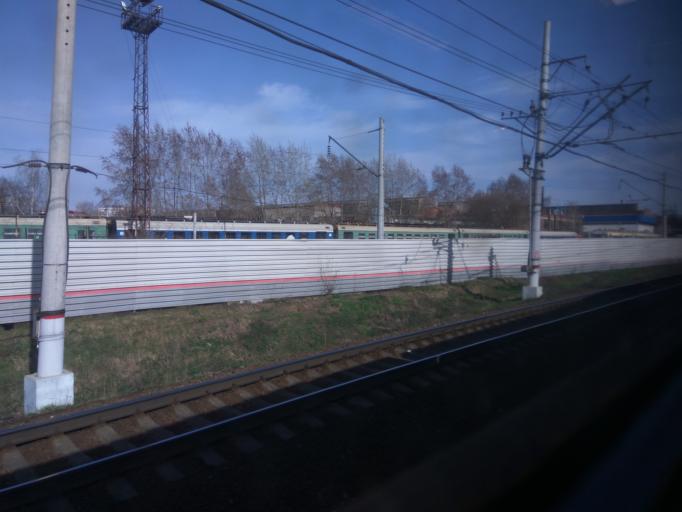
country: RU
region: Moscow
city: Ryazanskiy
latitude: 55.7433
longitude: 37.7433
